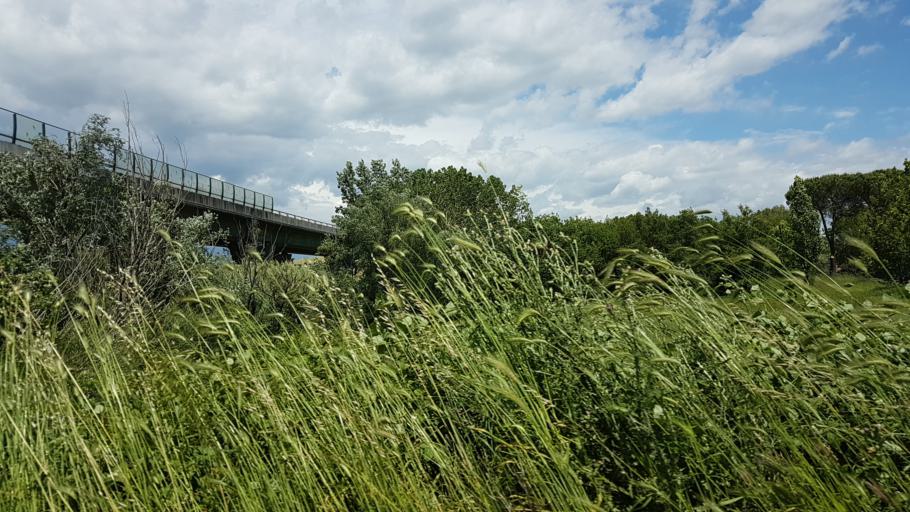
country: IT
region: Tuscany
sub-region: Provincia di Livorno
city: Rosignano Marittimo
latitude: 43.4375
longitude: 10.4878
